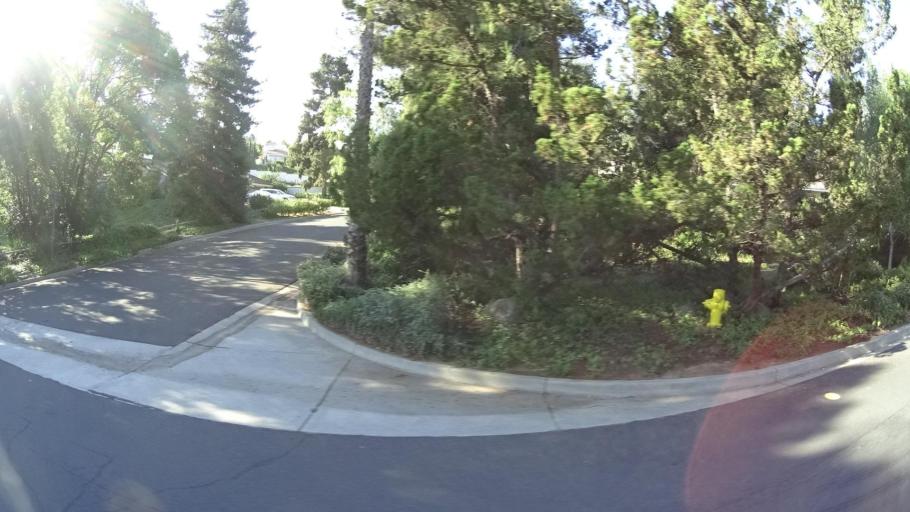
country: US
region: California
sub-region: San Diego County
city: Escondido
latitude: 33.0728
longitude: -117.0800
